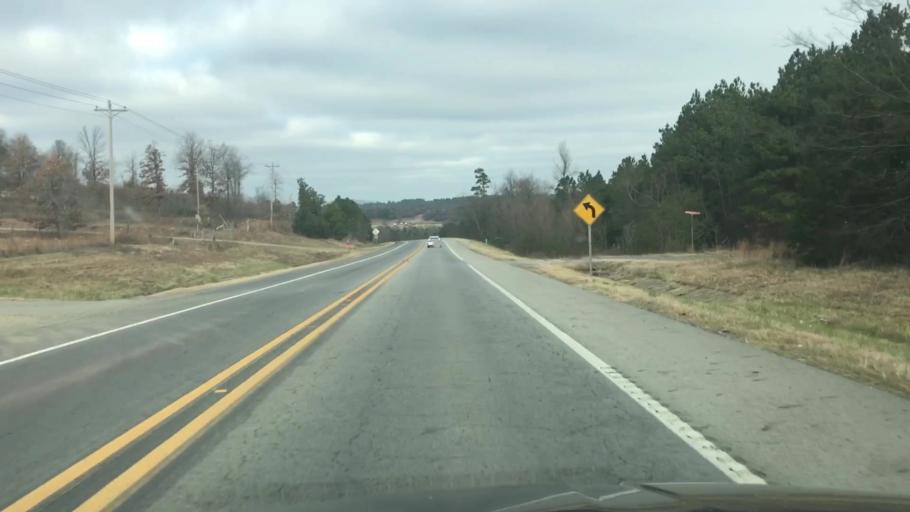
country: US
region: Arkansas
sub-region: Scott County
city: Waldron
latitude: 34.8414
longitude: -94.0537
